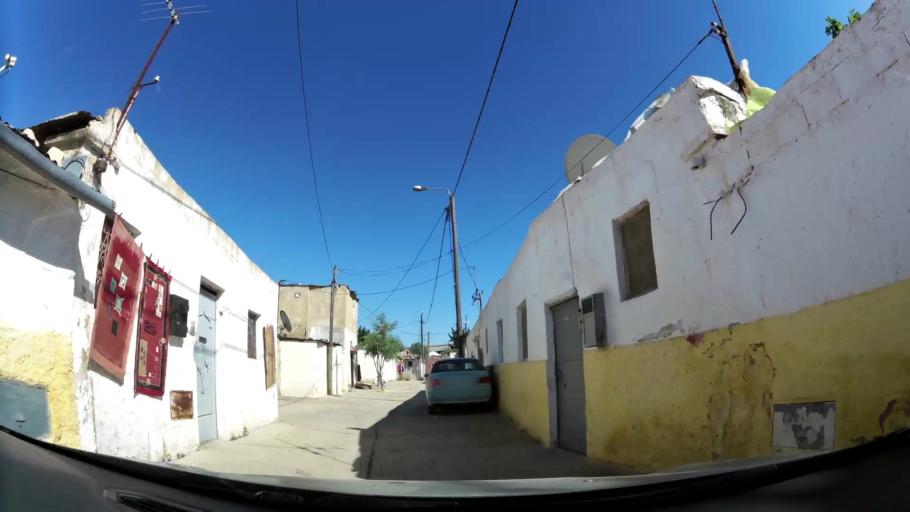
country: MA
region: Meknes-Tafilalet
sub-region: Meknes
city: Meknes
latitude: 33.8910
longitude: -5.5293
